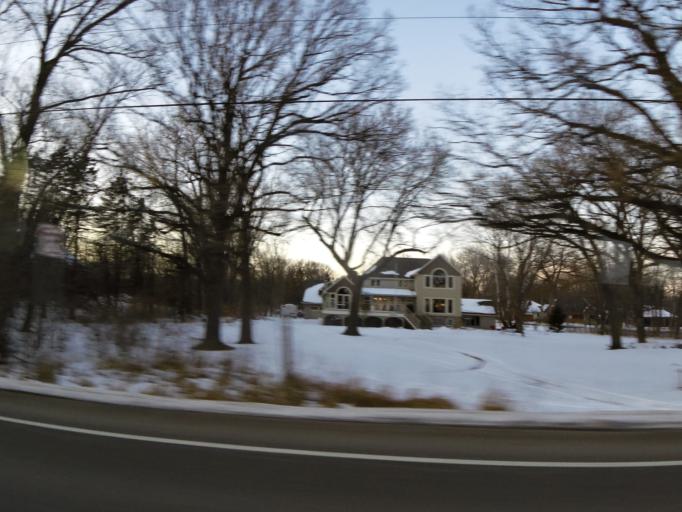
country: US
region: Minnesota
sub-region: Washington County
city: Dellwood
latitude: 45.0977
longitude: -92.9920
